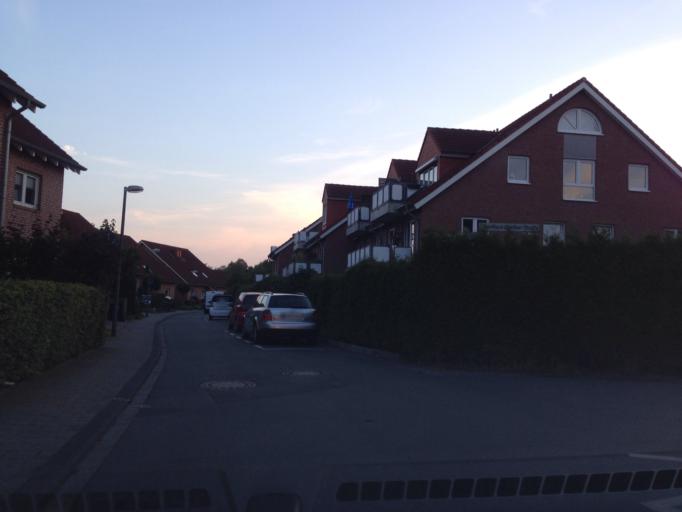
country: DE
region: North Rhine-Westphalia
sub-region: Regierungsbezirk Munster
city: Muenster
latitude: 51.9080
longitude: 7.6273
